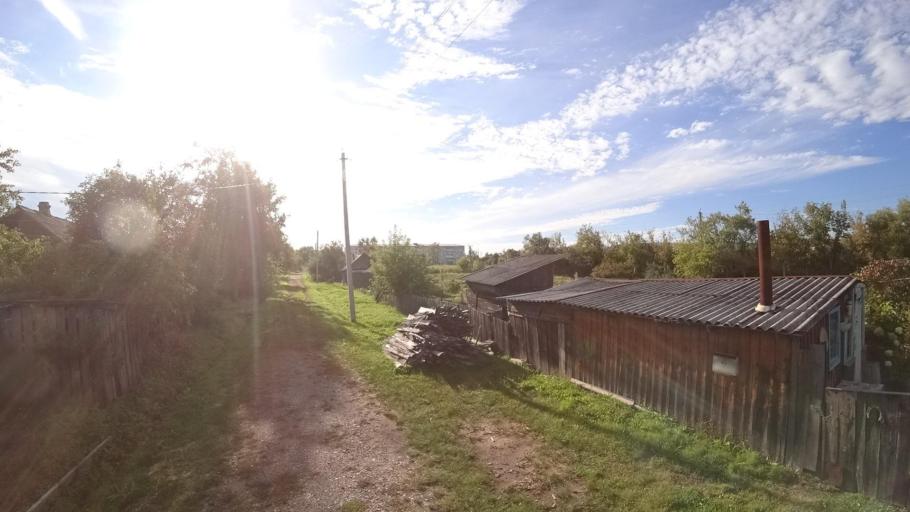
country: RU
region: Primorskiy
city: Dostoyevka
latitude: 44.2911
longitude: 133.4294
